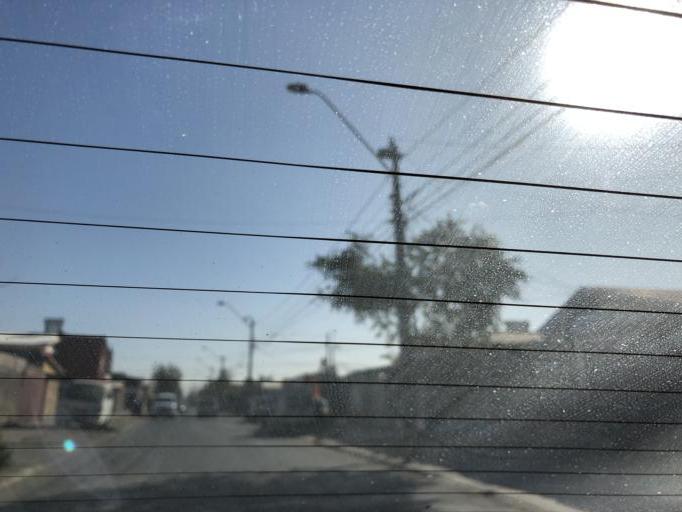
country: CL
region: Santiago Metropolitan
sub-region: Provincia de Cordillera
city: Puente Alto
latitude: -33.6220
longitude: -70.5923
